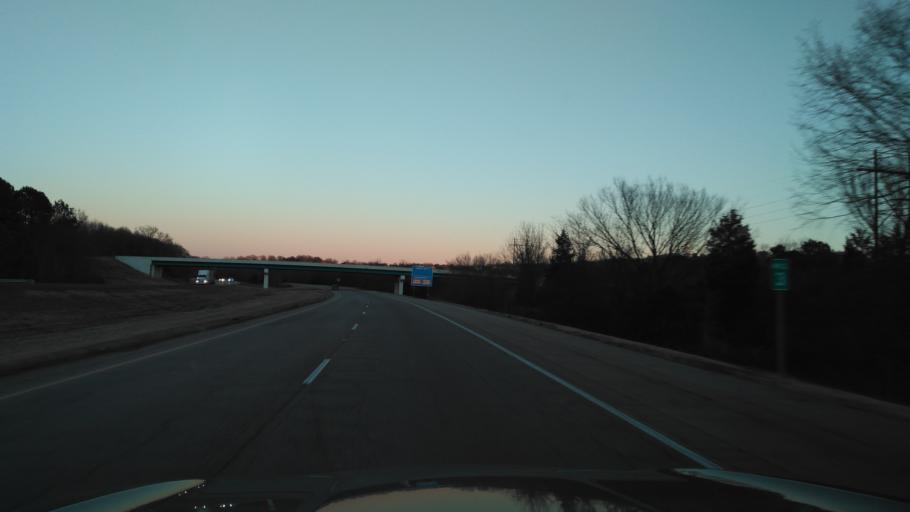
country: US
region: Arkansas
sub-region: Crawford County
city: Van Buren
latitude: 35.4592
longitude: -94.3942
